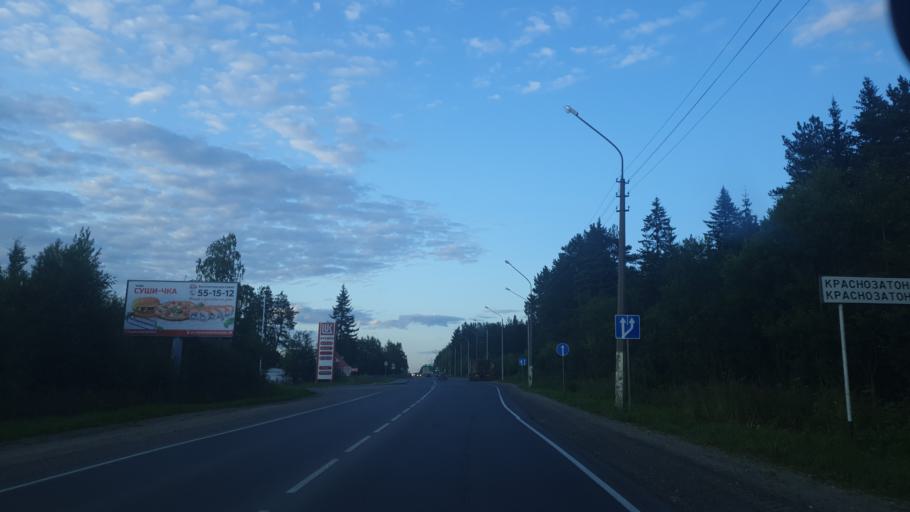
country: RU
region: Komi Republic
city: Verkhnyaya Maksakovka
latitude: 61.6635
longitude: 50.9684
